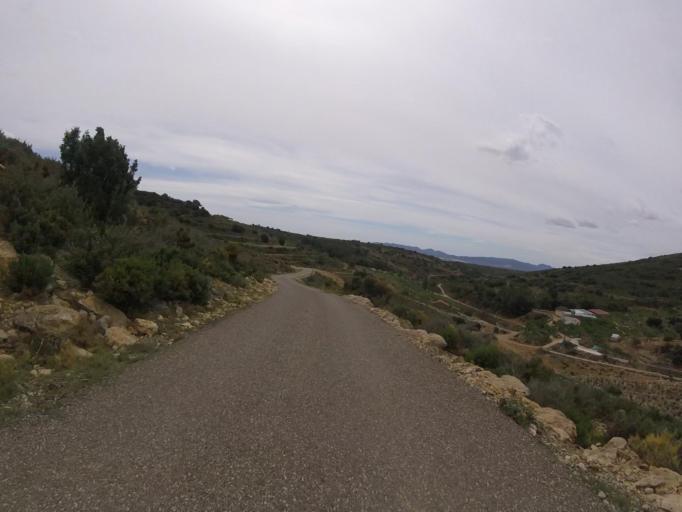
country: ES
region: Valencia
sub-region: Provincia de Castello
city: Sierra-Engarceran
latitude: 40.2640
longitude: -0.0232
